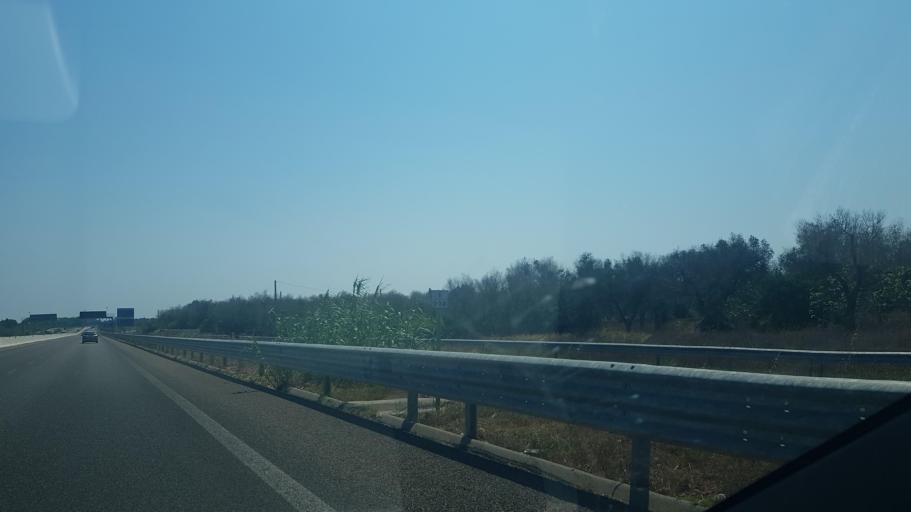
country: IT
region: Apulia
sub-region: Provincia di Lecce
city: Otranto
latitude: 40.1465
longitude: 18.4631
